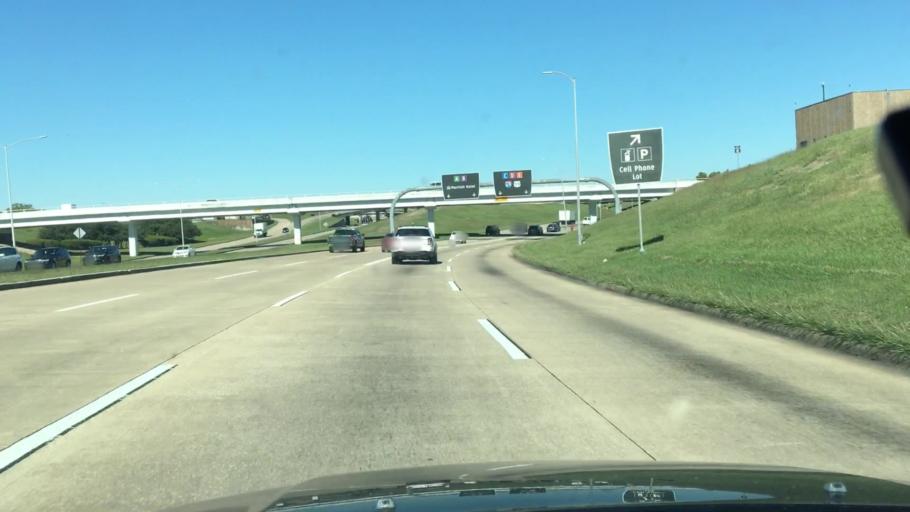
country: US
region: Texas
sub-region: Harris County
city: Aldine
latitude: 29.9767
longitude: -95.3425
